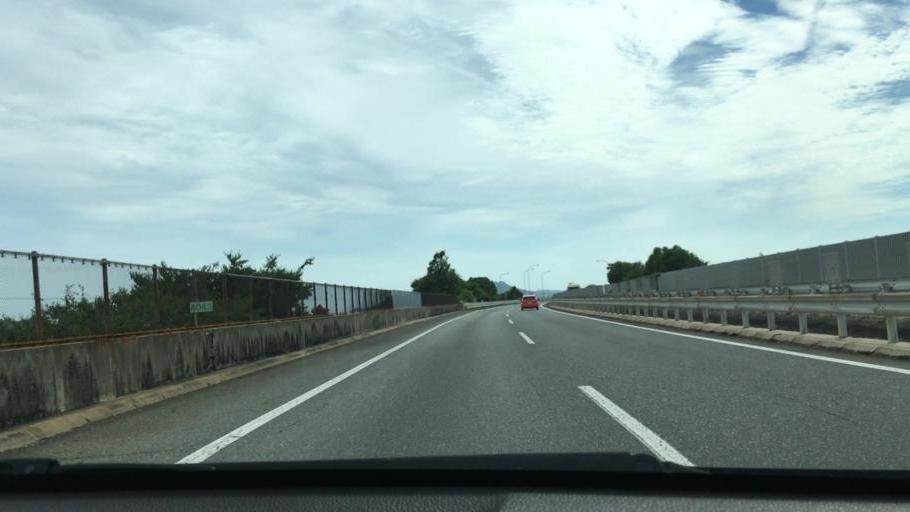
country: JP
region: Yamaguchi
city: Hofu
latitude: 34.0576
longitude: 131.5405
